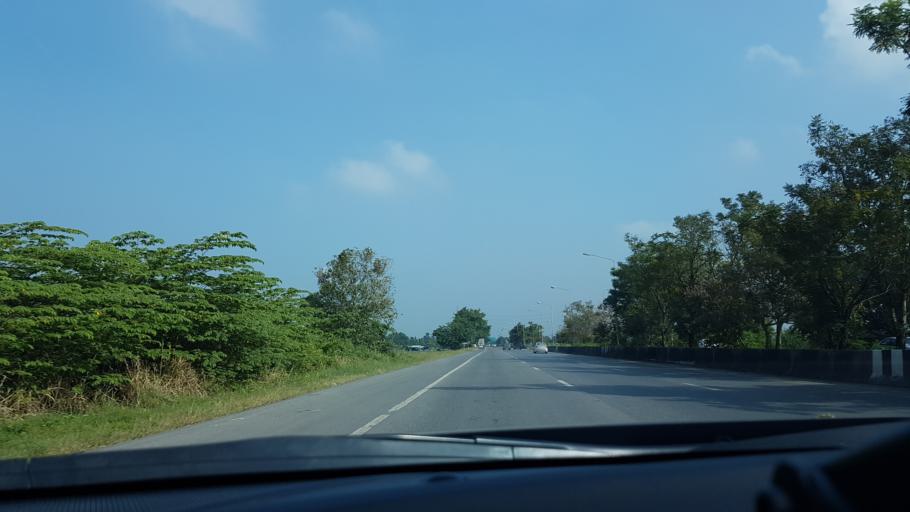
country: TH
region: Pathum Thani
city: Sam Khok
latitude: 14.1386
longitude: 100.5692
